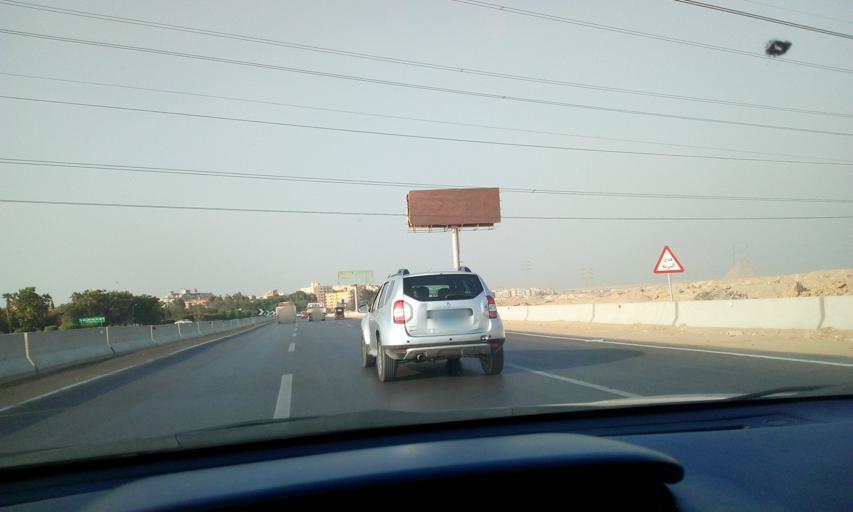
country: EG
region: Al Jizah
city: Al Jizah
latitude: 29.9418
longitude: 31.0982
